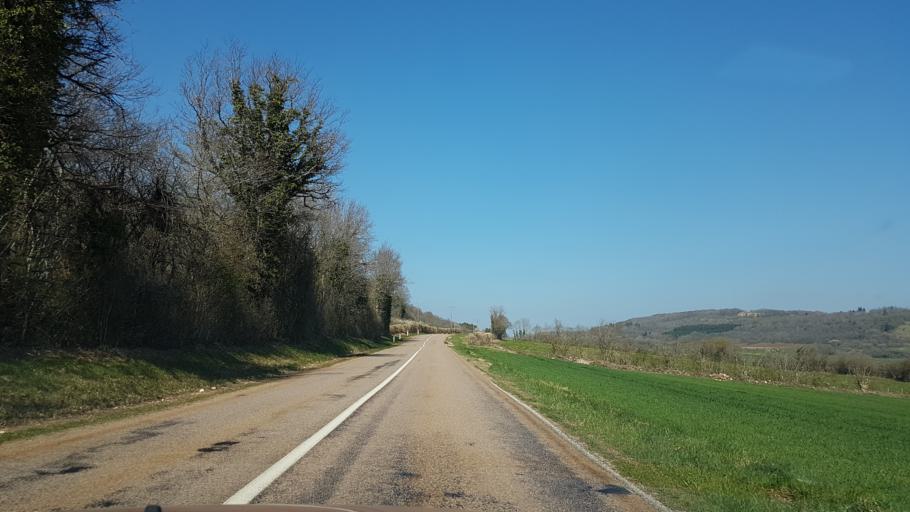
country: FR
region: Franche-Comte
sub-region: Departement du Jura
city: Orgelet
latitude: 46.5296
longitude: 5.6413
